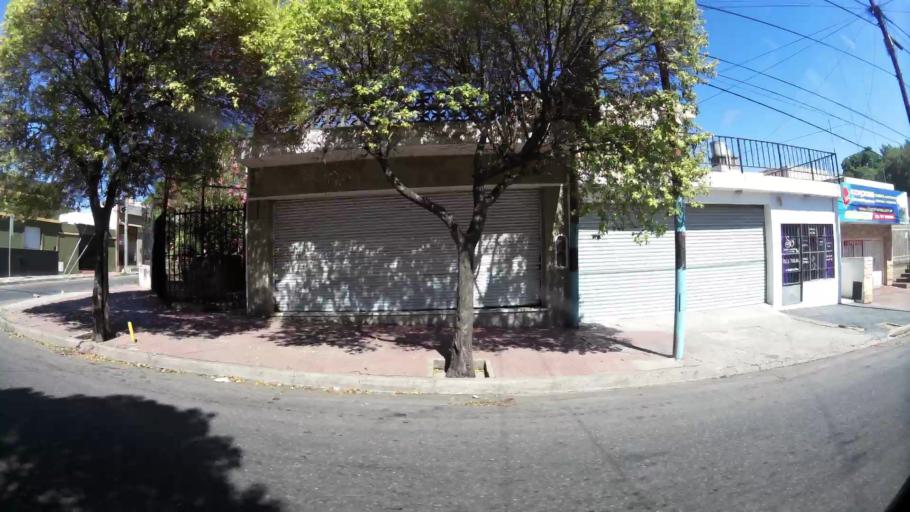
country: AR
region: Cordoba
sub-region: Departamento de Capital
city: Cordoba
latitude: -31.4321
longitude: -64.1517
